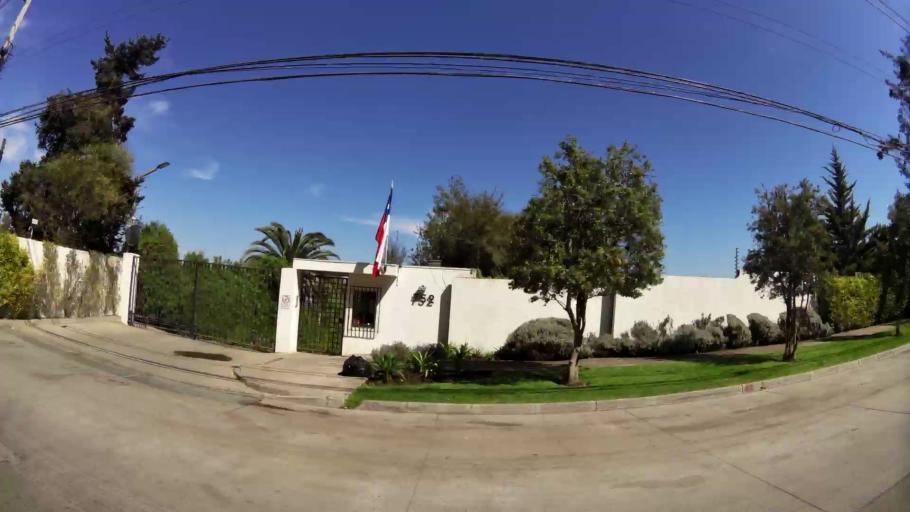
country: CL
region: Santiago Metropolitan
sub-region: Provincia de Santiago
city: Villa Presidente Frei, Nunoa, Santiago, Chile
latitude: -33.4479
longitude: -70.5195
